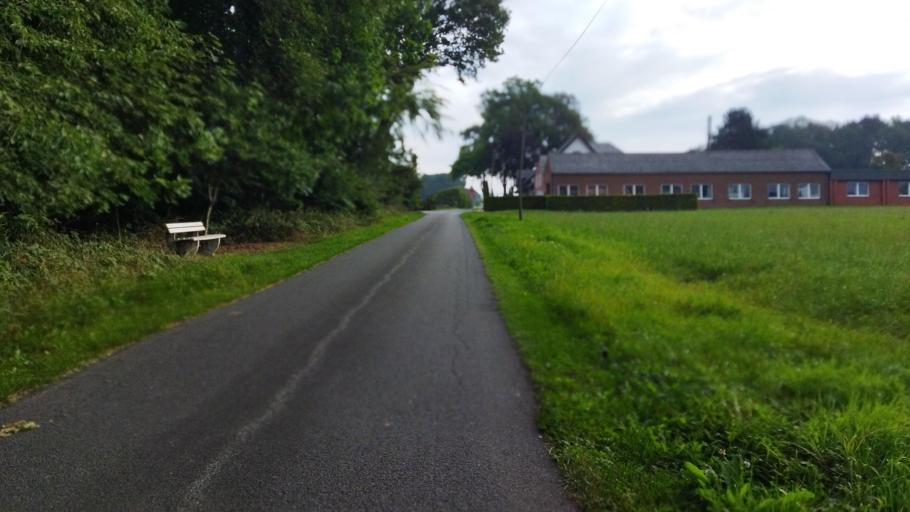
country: DE
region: Lower Saxony
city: Bad Laer
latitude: 52.0769
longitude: 8.1164
